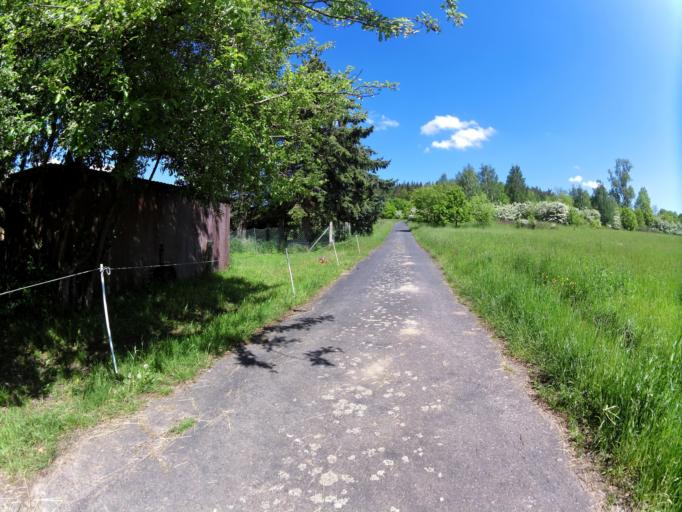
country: DE
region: Thuringia
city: Dankmarshausen
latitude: 50.9560
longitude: 10.0279
